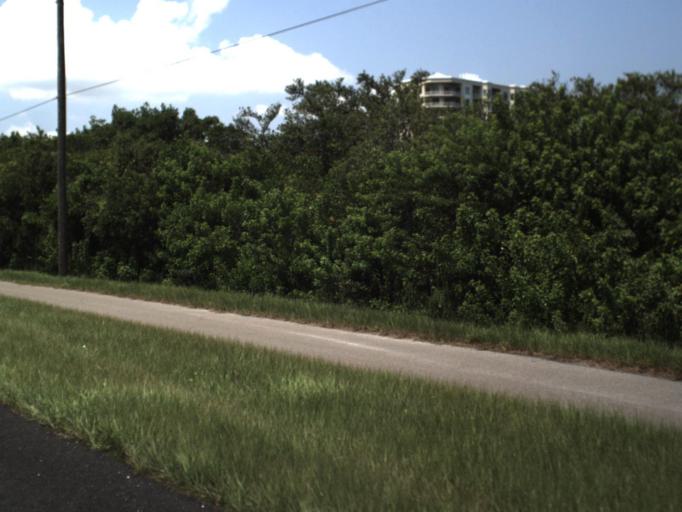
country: US
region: Florida
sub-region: Pinellas County
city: Gandy
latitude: 27.8695
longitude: -82.6188
